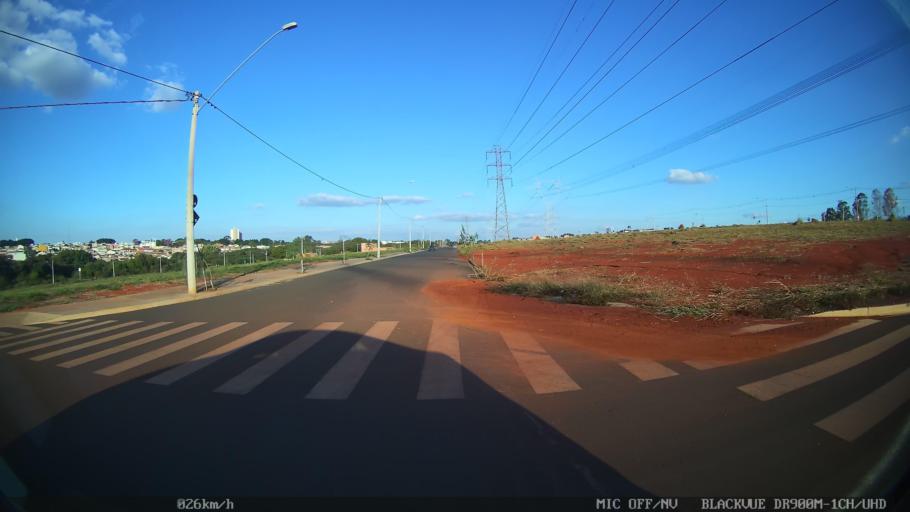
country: BR
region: Sao Paulo
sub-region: Santa Barbara D'Oeste
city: Santa Barbara d'Oeste
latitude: -22.7449
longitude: -47.3884
